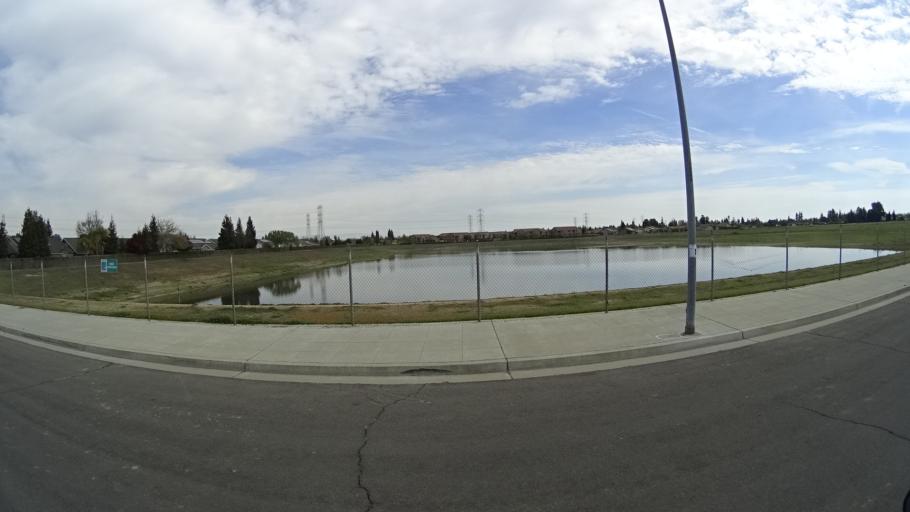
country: US
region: California
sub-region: Fresno County
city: West Park
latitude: 36.8184
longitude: -119.8807
